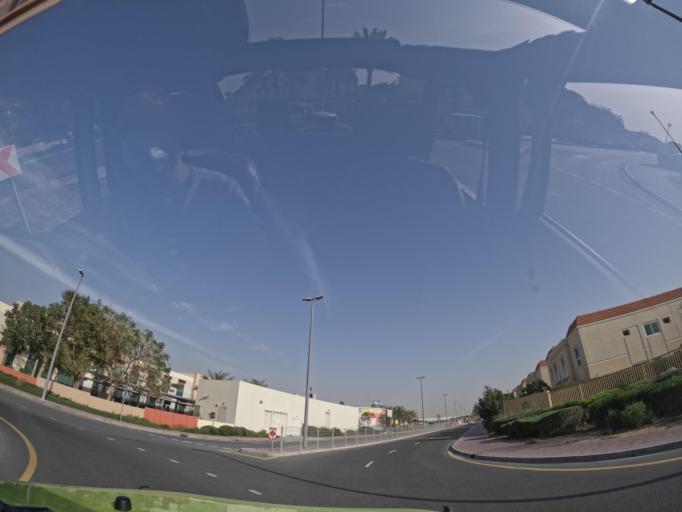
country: AE
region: Dubai
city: Dubai
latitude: 25.1247
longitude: 55.3574
